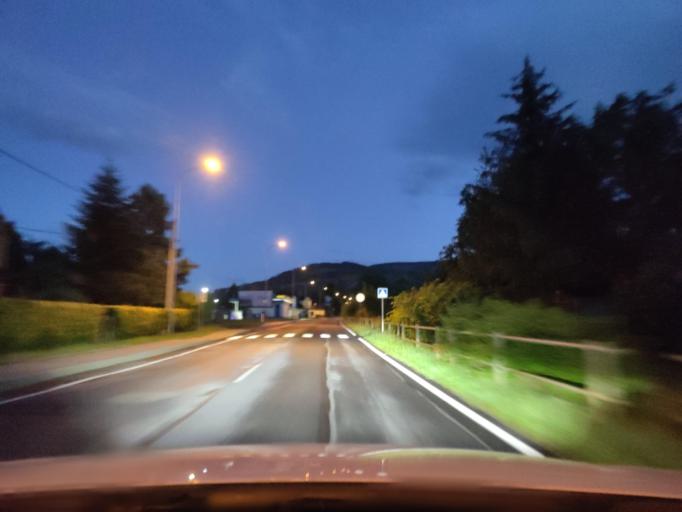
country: CZ
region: Olomoucky
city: Zlate Hory
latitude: 50.2561
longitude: 17.3998
